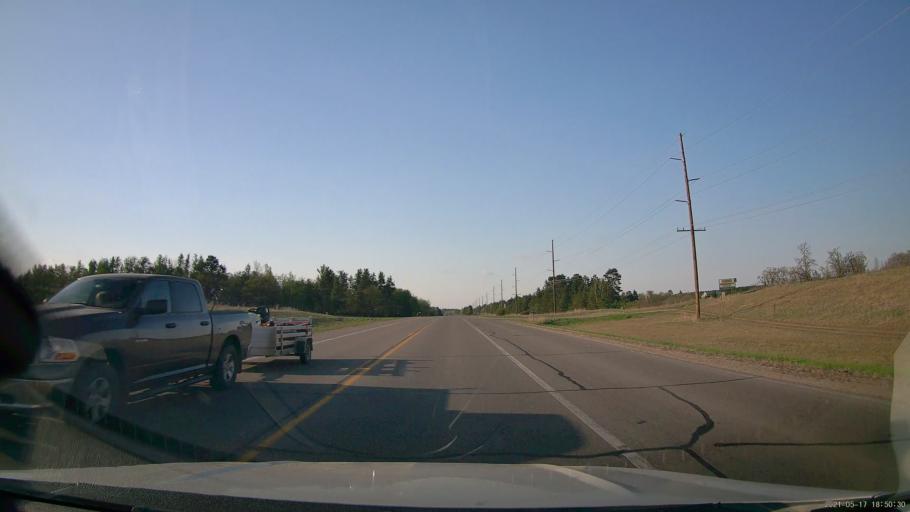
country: US
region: Minnesota
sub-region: Hubbard County
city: Park Rapids
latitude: 46.9353
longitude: -95.0168
